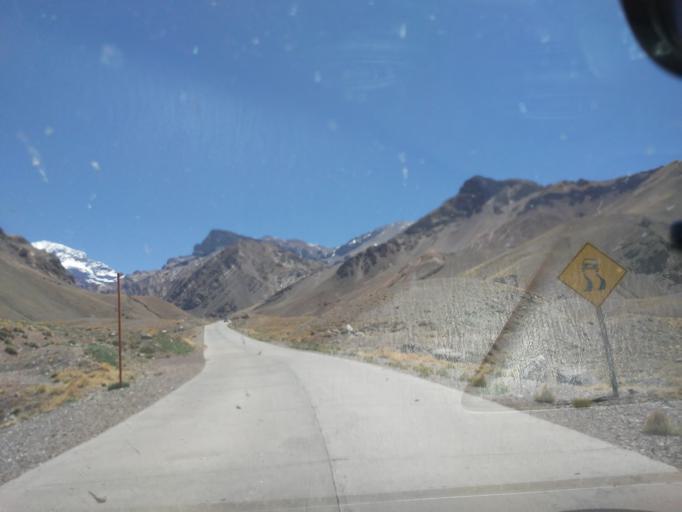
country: CL
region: Valparaiso
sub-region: Provincia de Los Andes
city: Los Andes
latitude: -32.8217
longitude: -69.9421
